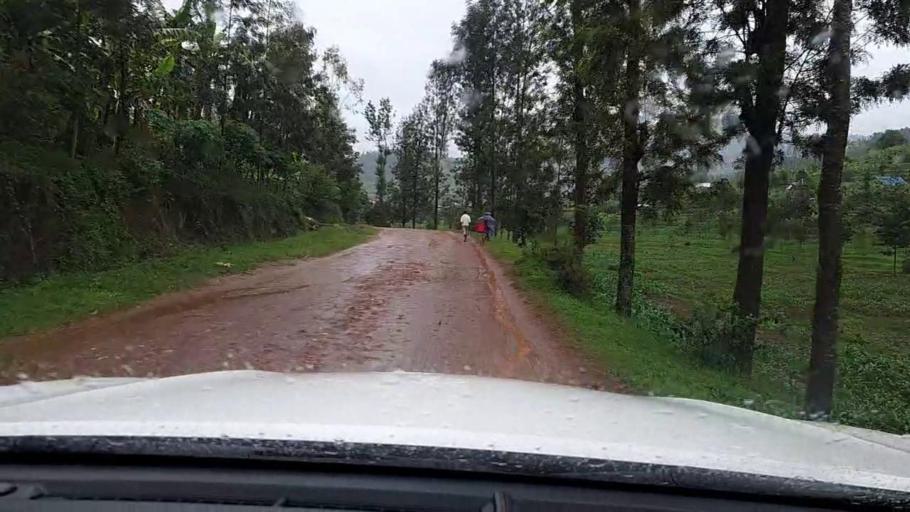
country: RW
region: Northern Province
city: Byumba
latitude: -1.7270
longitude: 29.9348
